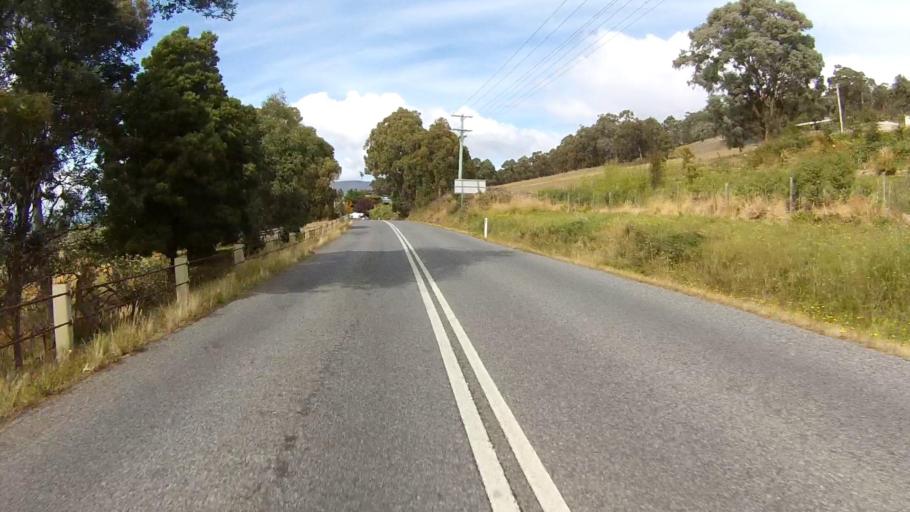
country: AU
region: Tasmania
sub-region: Kingborough
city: Kettering
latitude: -43.1403
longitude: 147.2438
